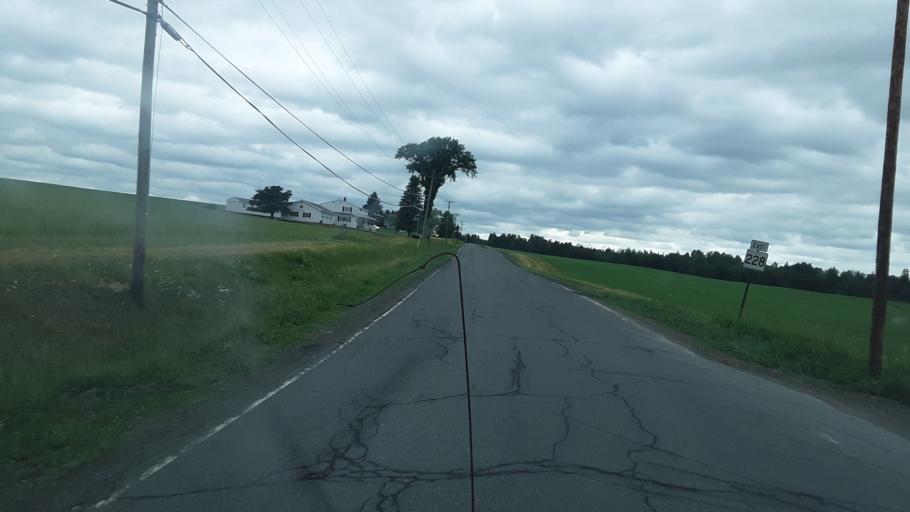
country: US
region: Maine
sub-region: Aroostook County
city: Caribou
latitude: 46.8071
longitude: -68.1564
